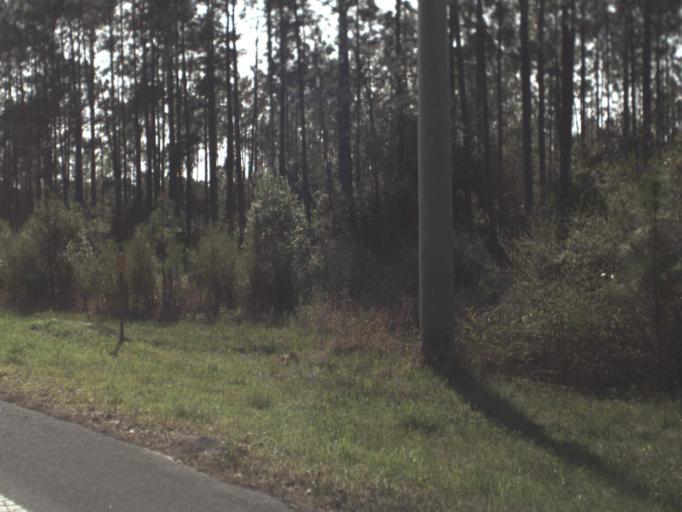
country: US
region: Florida
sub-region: Franklin County
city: Carrabelle
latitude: 29.9601
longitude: -84.5032
